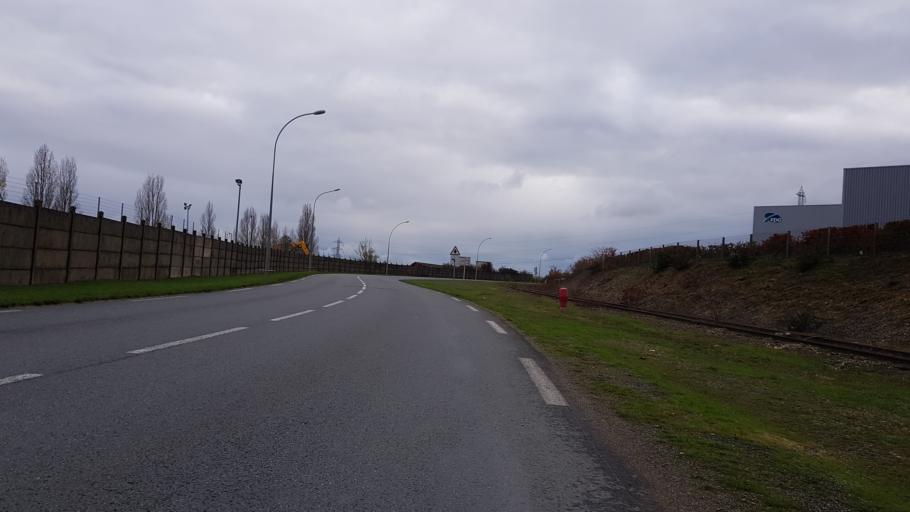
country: FR
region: Poitou-Charentes
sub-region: Departement de la Vienne
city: Chasseneuil-du-Poitou
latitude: 46.6652
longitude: 0.3759
